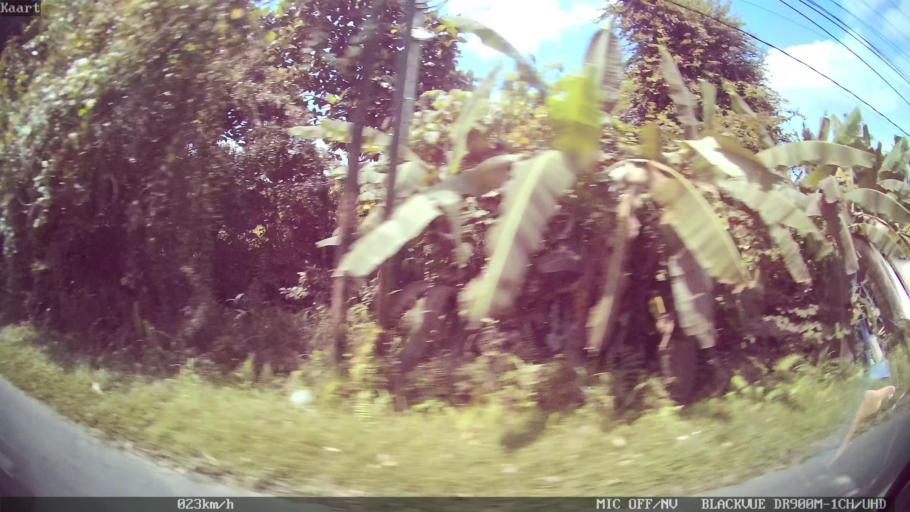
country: ID
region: Bali
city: Banjar Kelodan
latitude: -8.5149
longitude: 115.3798
